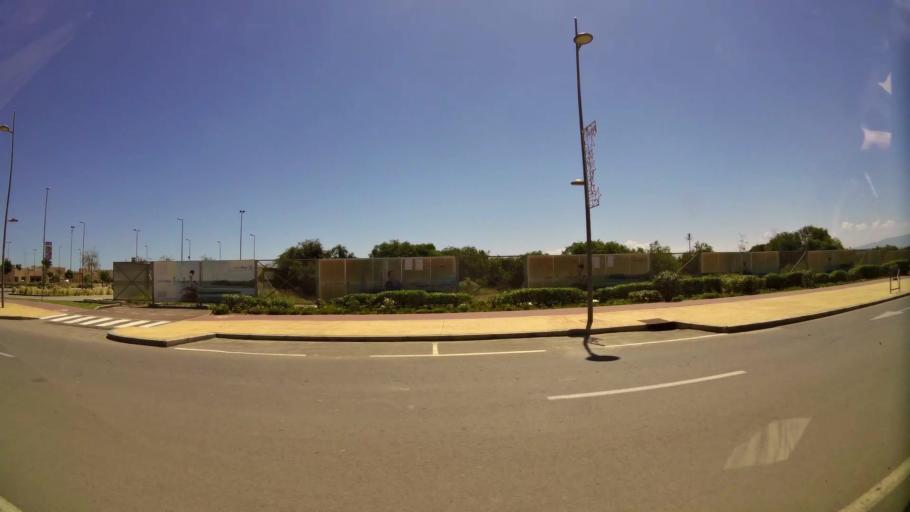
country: MA
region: Oriental
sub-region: Berkane-Taourirt
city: Madagh
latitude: 35.1055
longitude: -2.3001
